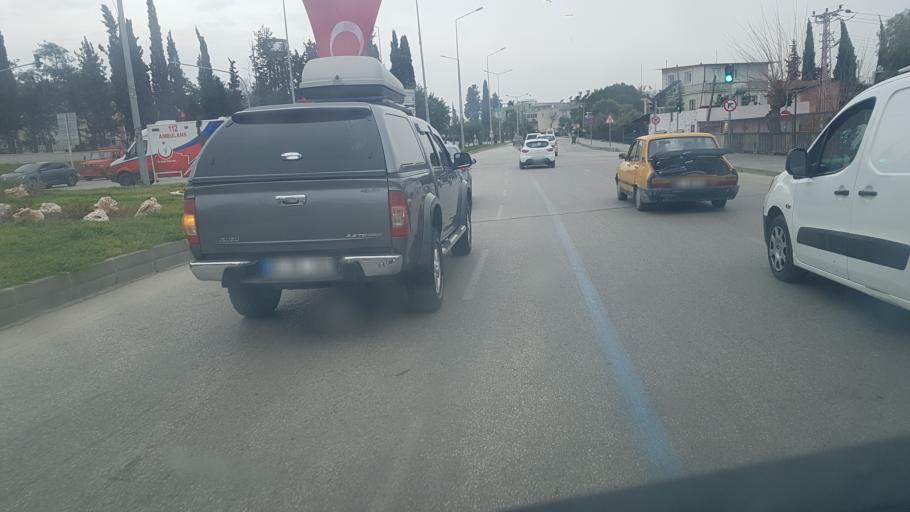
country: TR
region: Adana
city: Adana
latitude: 37.0143
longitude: 35.3388
